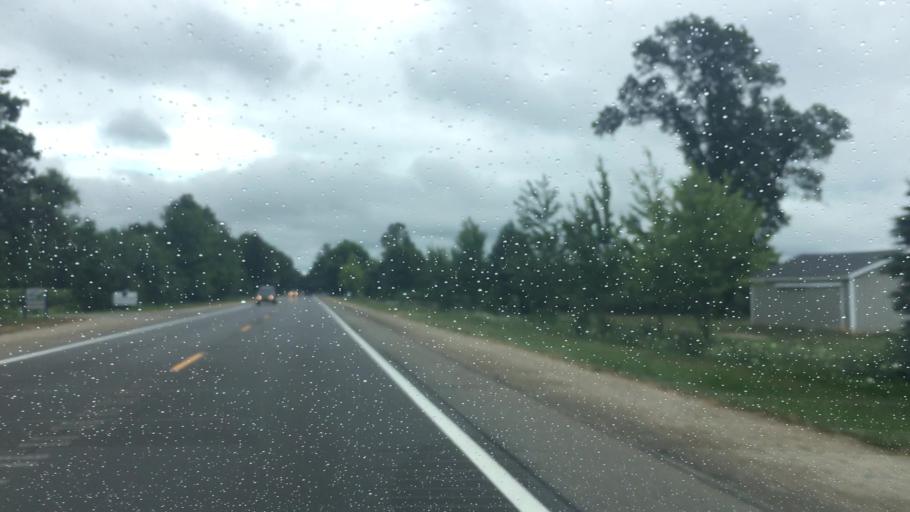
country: US
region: Michigan
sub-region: Ottawa County
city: Spring Lake
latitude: 42.9722
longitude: -86.1529
